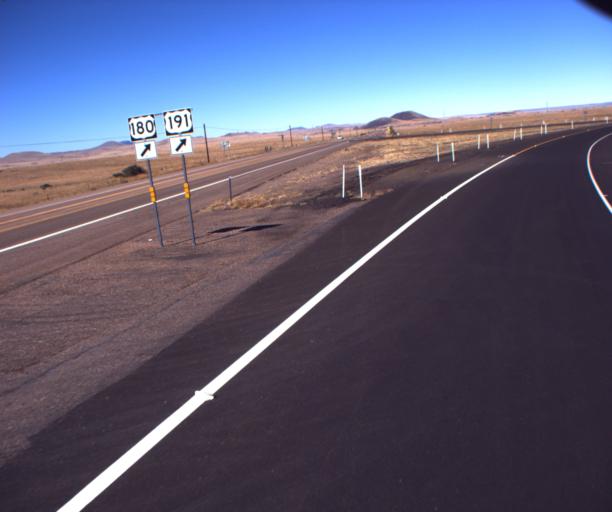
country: US
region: Arizona
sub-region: Apache County
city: Springerville
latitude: 34.1730
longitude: -109.3168
